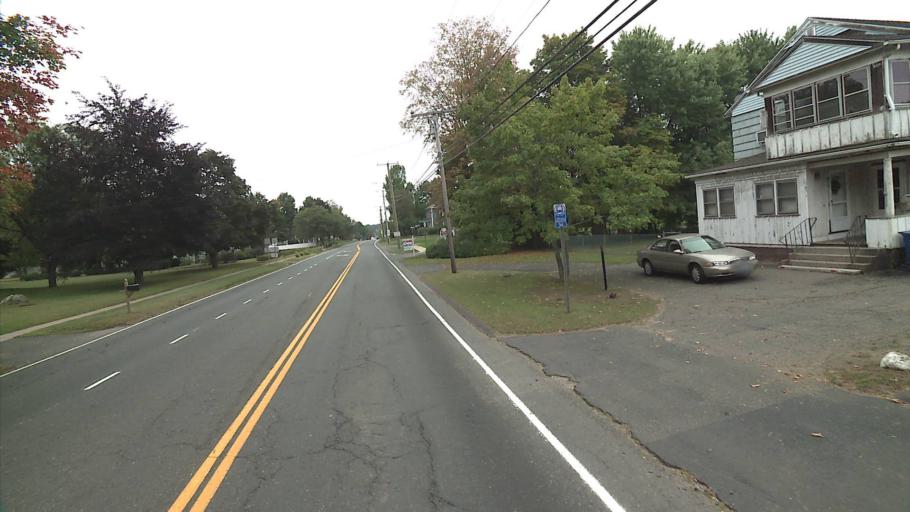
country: US
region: Connecticut
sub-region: Hartford County
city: Windsor Locks
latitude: 41.9077
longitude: -72.6791
